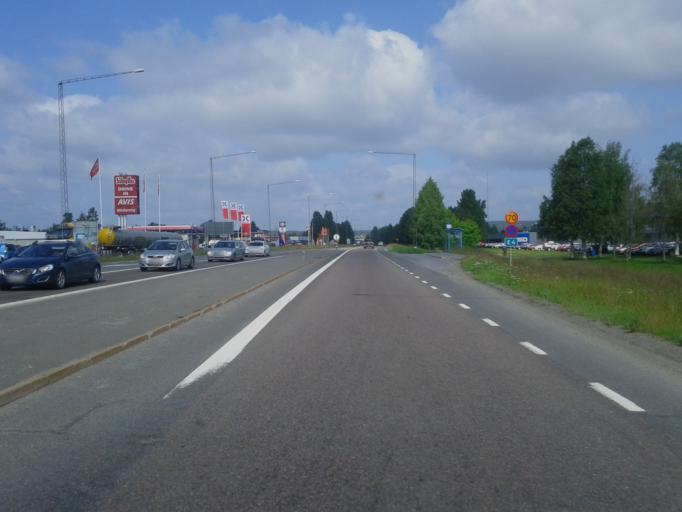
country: SE
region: Vaesterbotten
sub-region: Skelleftea Kommun
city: Skelleftea
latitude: 64.7371
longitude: 20.9661
